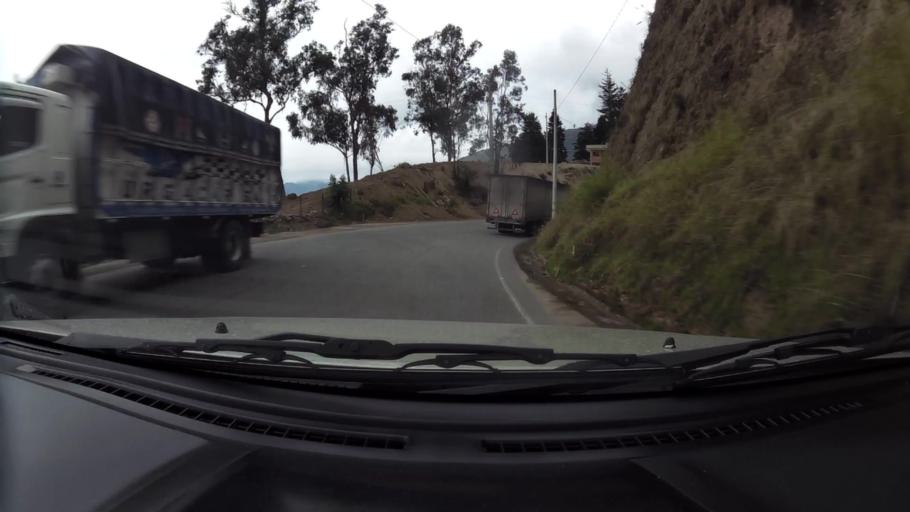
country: EC
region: Chimborazo
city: Alausi
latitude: -2.3043
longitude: -78.9184
